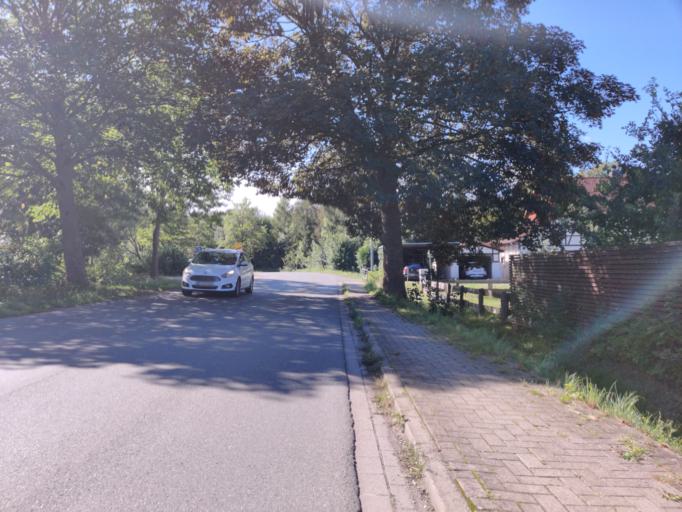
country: DE
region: Lower Saxony
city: Holle
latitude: 52.1062
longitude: 10.1645
